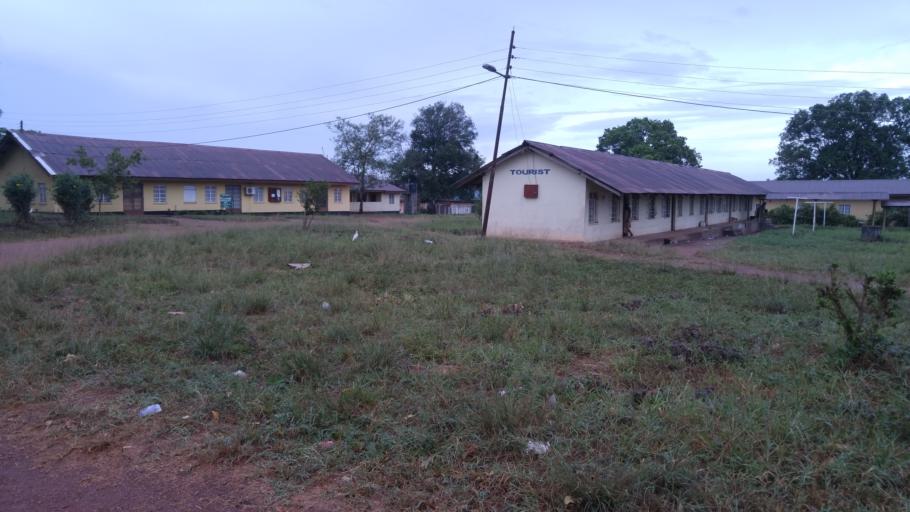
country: SL
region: Southern Province
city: Largo
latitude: 8.1145
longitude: -12.0704
